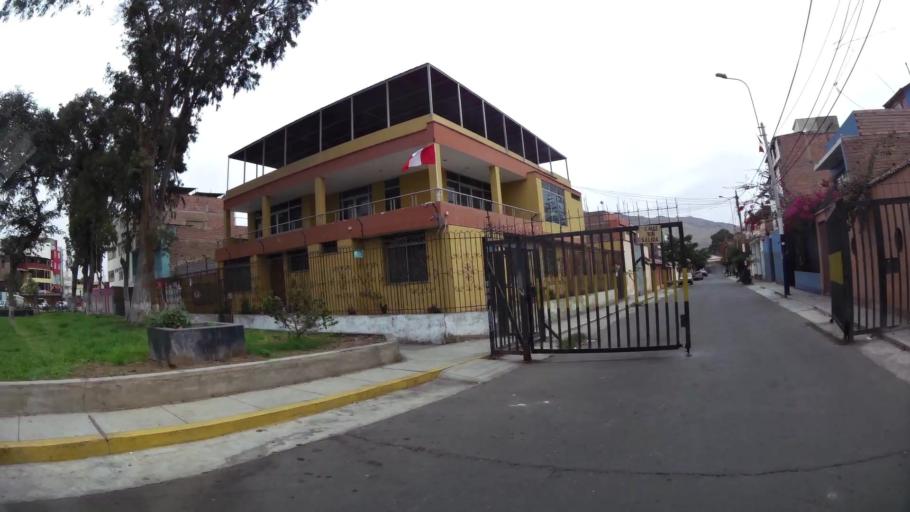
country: PE
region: Lima
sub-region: Lima
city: Surco
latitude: -12.1692
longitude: -77.0194
